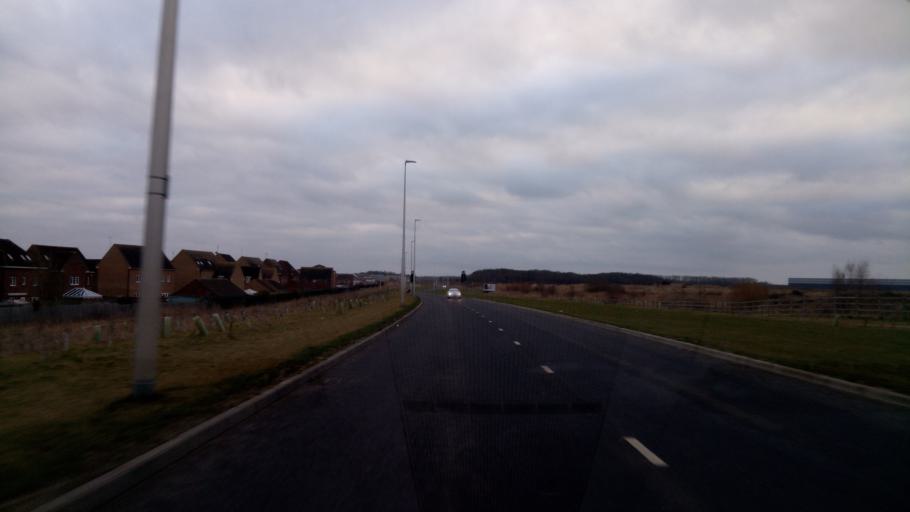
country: GB
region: England
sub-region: Cambridgeshire
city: Yaxley
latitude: 52.5372
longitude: -0.2818
